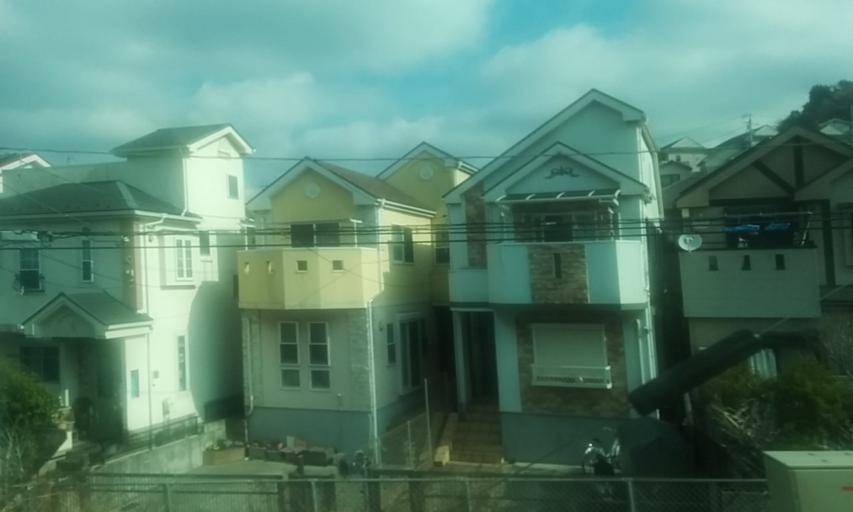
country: JP
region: Kanagawa
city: Yokohama
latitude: 35.4471
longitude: 139.5796
